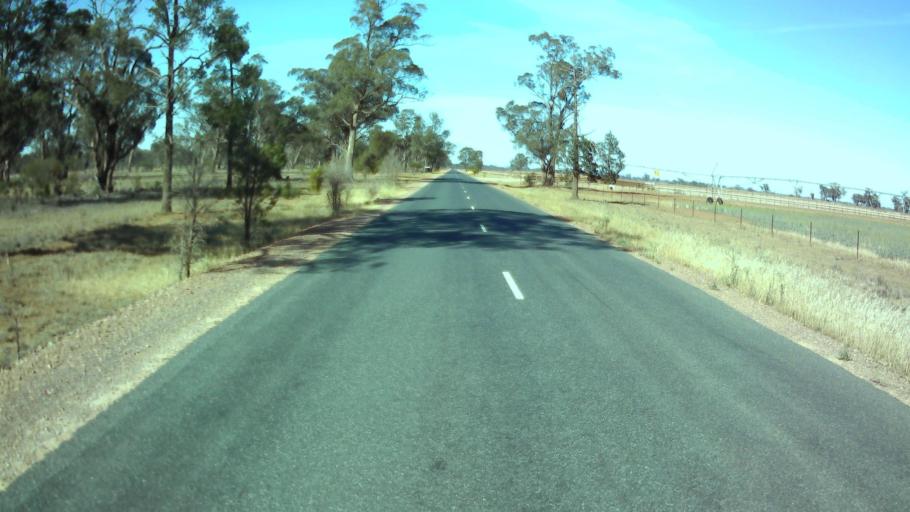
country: AU
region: New South Wales
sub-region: Weddin
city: Grenfell
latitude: -34.1168
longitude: 147.8178
